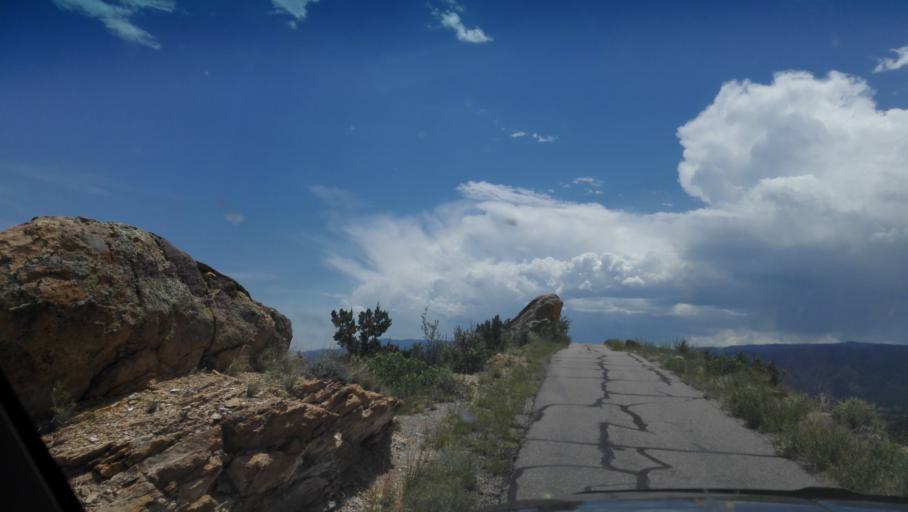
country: US
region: Colorado
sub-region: Fremont County
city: Canon City
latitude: 38.4540
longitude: -105.2496
